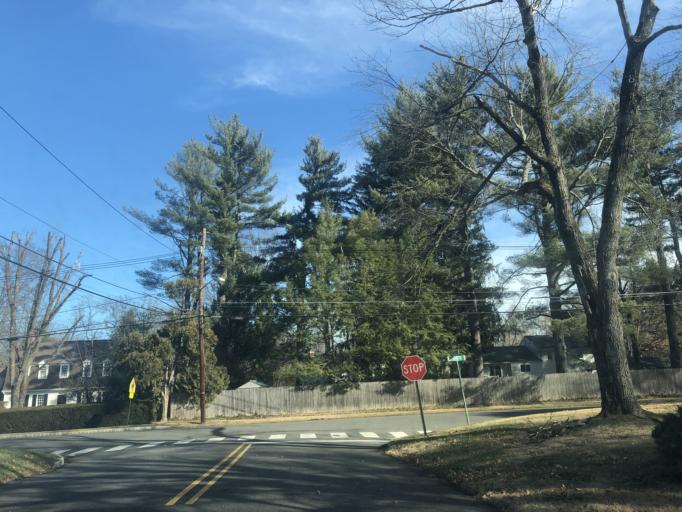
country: US
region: New Jersey
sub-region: Mercer County
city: Princeton
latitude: 40.3525
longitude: -74.6365
